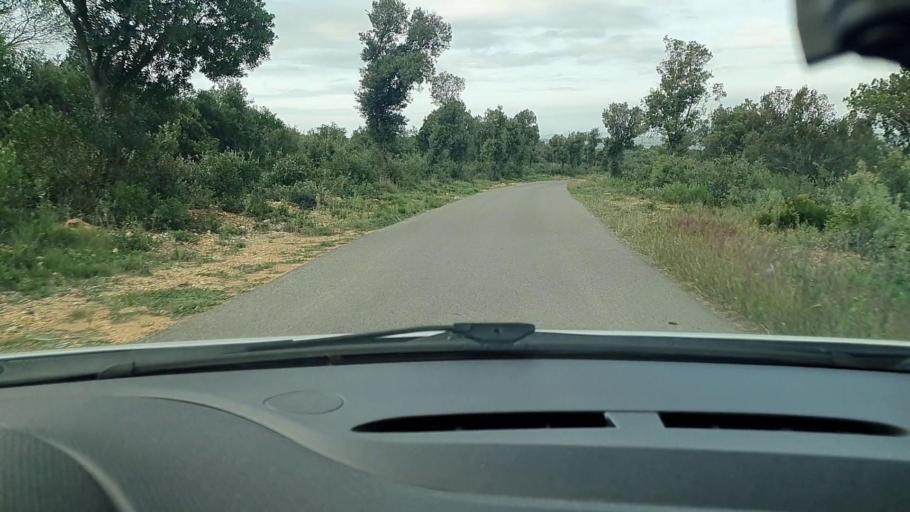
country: FR
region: Languedoc-Roussillon
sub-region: Departement du Gard
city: Mons
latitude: 44.1442
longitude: 4.2567
